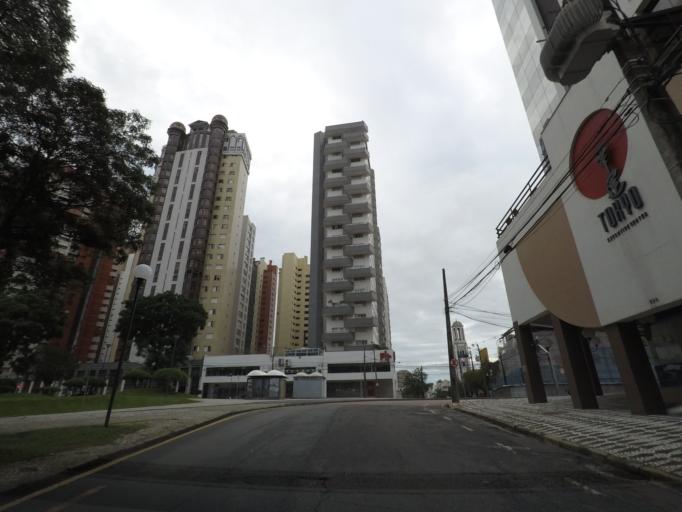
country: BR
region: Parana
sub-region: Curitiba
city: Curitiba
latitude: -25.4457
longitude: -49.2865
